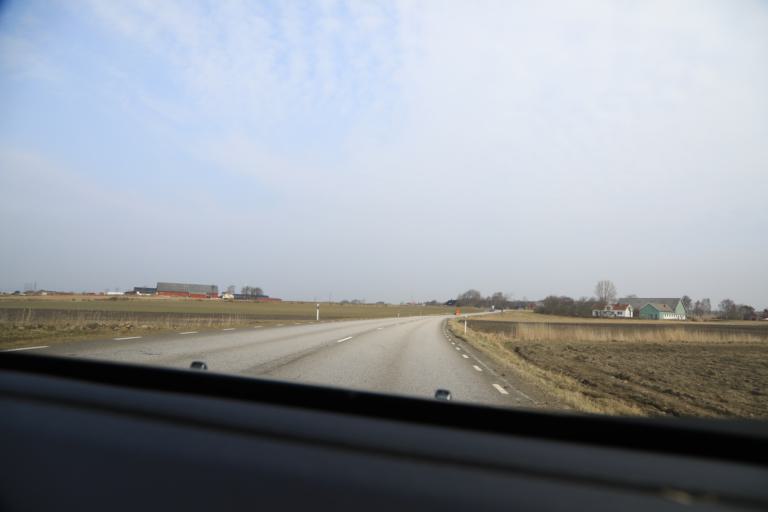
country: SE
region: Halland
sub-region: Kungsbacka Kommun
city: Frillesas
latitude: 57.2637
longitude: 12.1790
